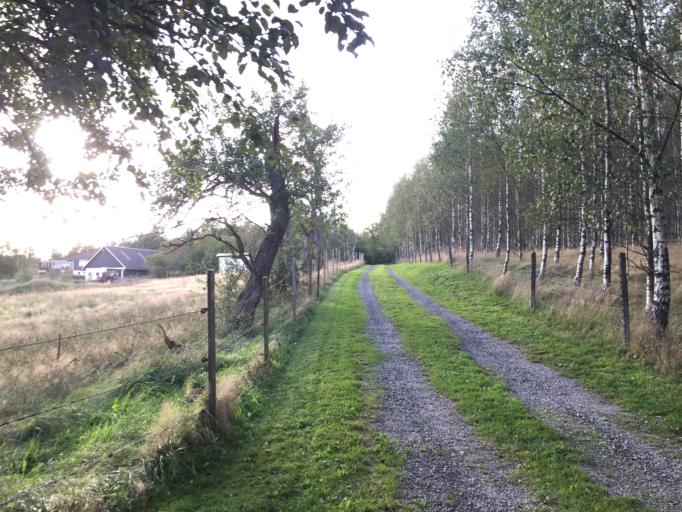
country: SE
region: Skane
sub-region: Perstorps Kommun
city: Perstorp
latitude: 56.2090
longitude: 13.3363
